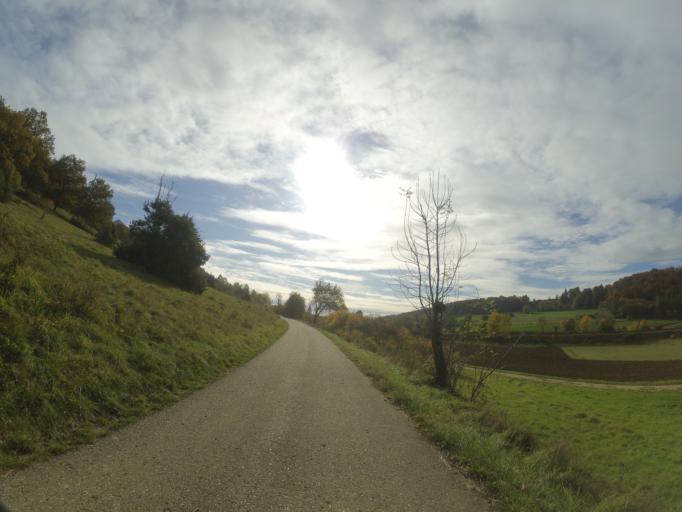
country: DE
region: Baden-Wuerttemberg
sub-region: Tuebingen Region
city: Lonsee
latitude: 48.5500
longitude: 9.9114
